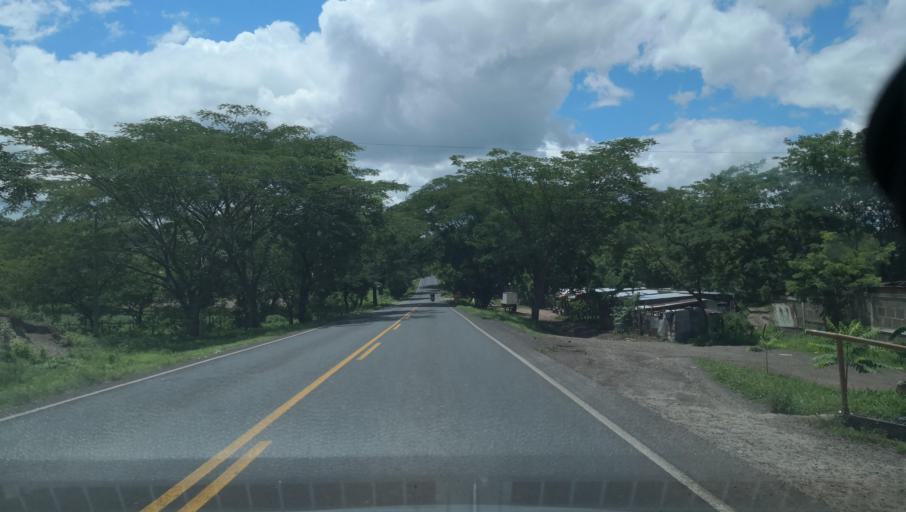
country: NI
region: Esteli
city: Condega
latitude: 13.3823
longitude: -86.4015
